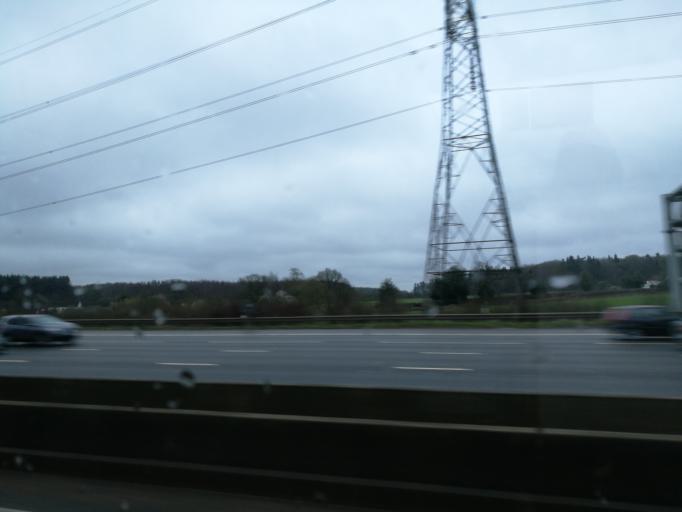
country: GB
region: England
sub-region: Hertfordshire
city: Abbots Langley
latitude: 51.7373
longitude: -0.3939
